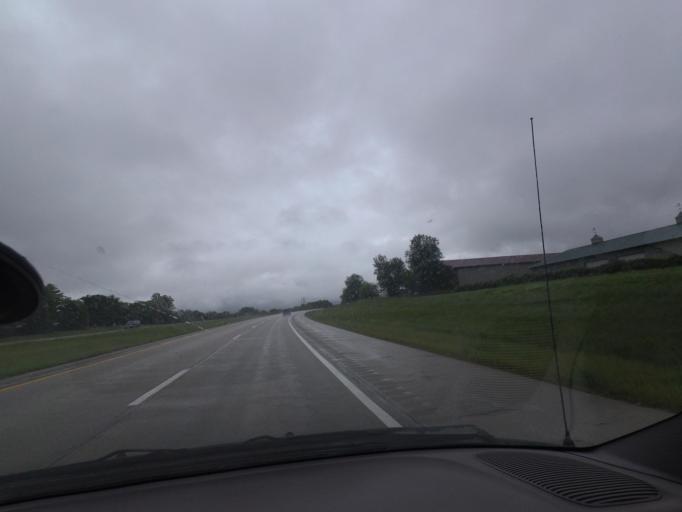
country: US
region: Illinois
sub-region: Champaign County
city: Champaign
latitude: 40.1196
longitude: -88.2922
